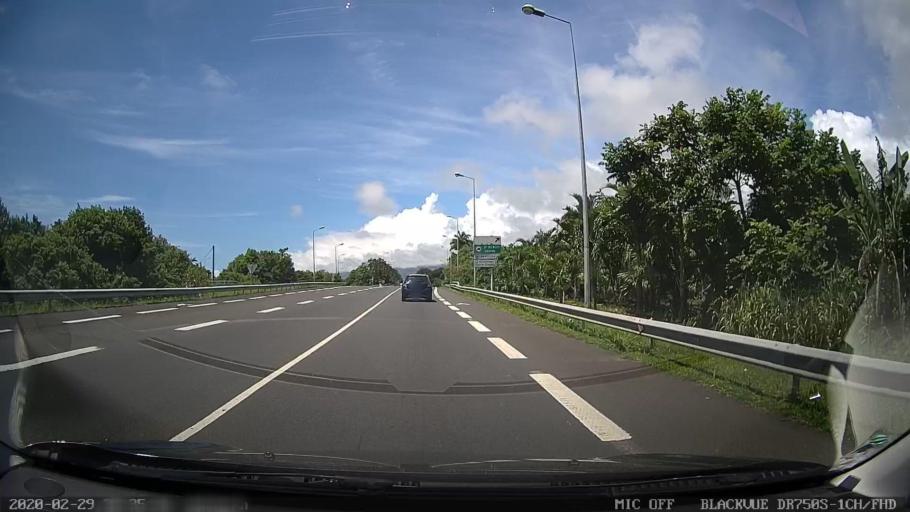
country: RE
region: Reunion
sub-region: Reunion
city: Saint-Benoit
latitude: -21.0330
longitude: 55.7055
